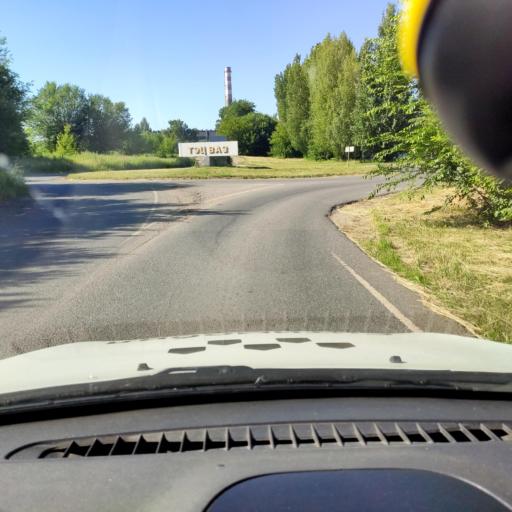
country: RU
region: Samara
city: Tol'yatti
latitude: 53.5750
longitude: 49.2547
